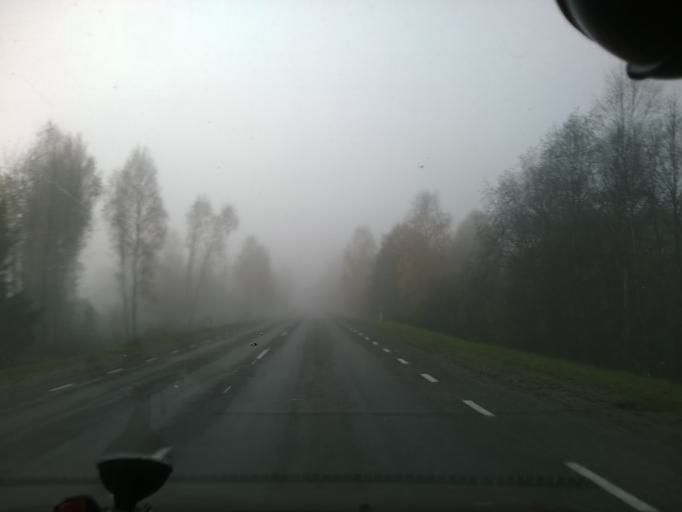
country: EE
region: Tartu
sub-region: Elva linn
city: Elva
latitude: 58.1424
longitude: 26.5223
